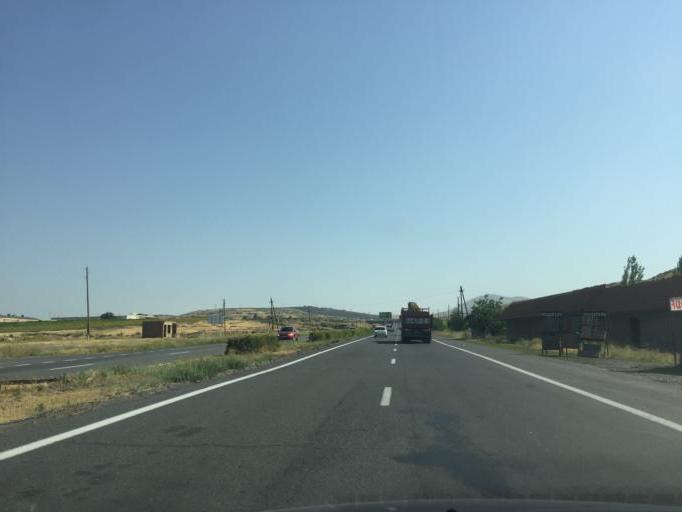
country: AM
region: Kotayk'i Marz
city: Arzni
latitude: 40.2951
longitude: 44.6133
